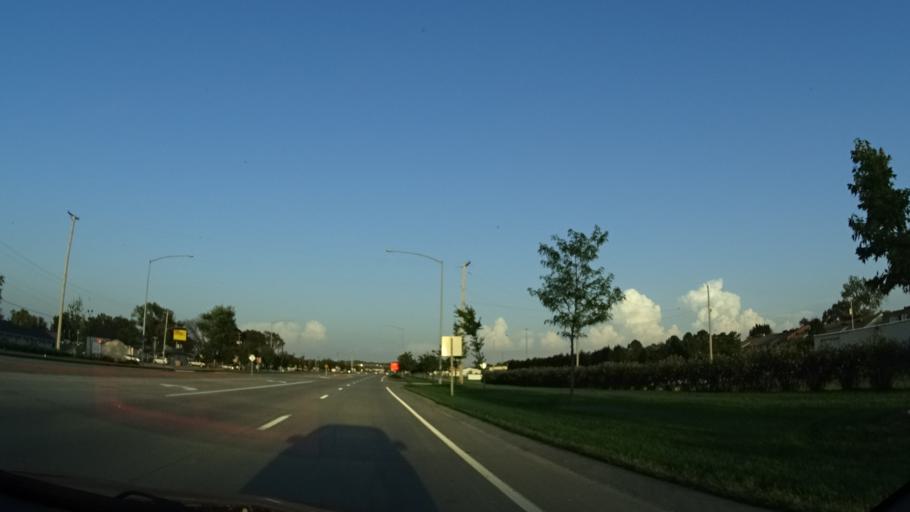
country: US
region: Iowa
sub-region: Pottawattamie County
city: Council Bluffs
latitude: 41.2195
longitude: -95.8567
